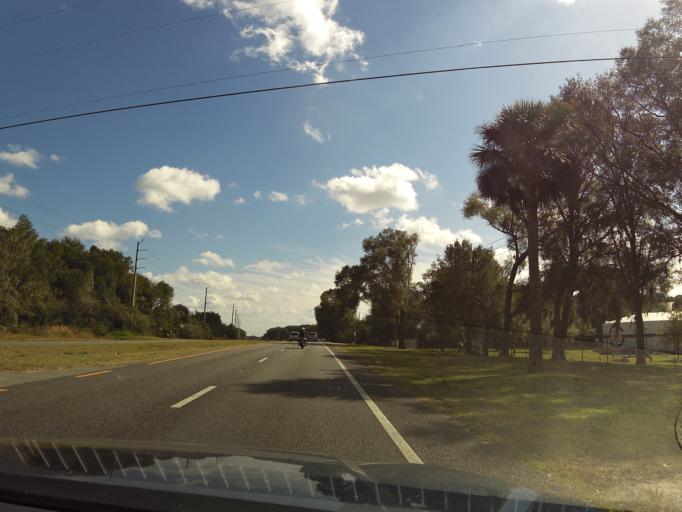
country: US
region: Florida
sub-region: Volusia County
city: North DeLand
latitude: 29.0806
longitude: -81.3168
